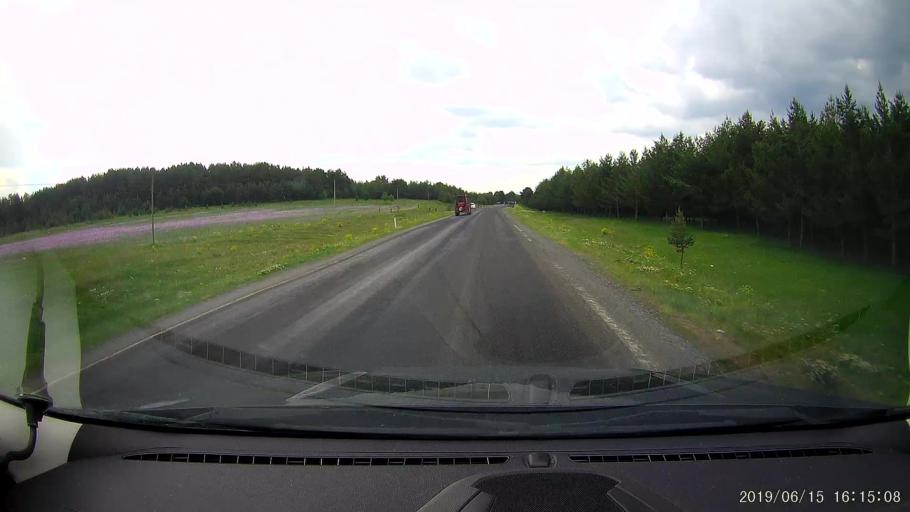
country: TR
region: Ardahan
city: Hanak
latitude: 41.2718
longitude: 42.8535
